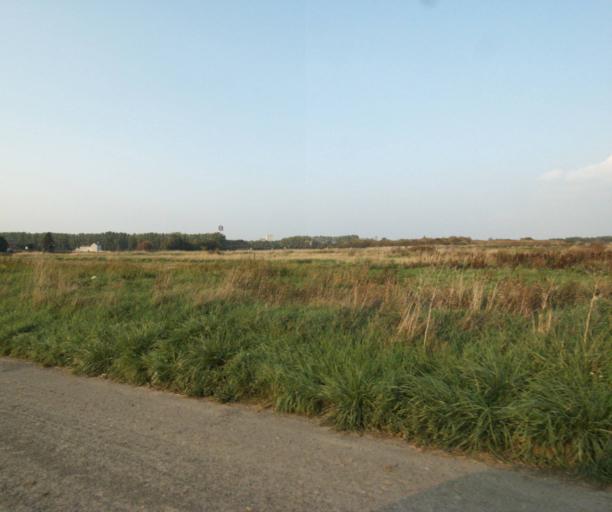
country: FR
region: Nord-Pas-de-Calais
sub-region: Departement du Nord
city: Emmerin
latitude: 50.5950
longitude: 3.0086
